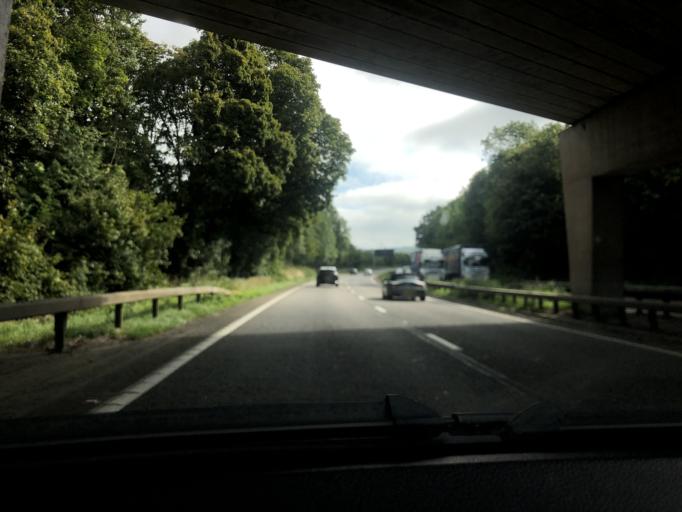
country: GB
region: England
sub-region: Devon
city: Honiton
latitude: 50.8023
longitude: -3.1992
